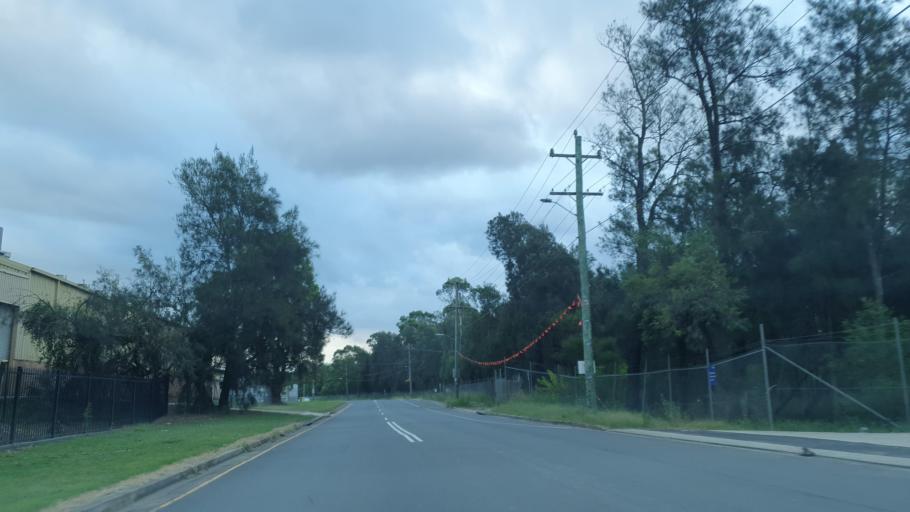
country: AU
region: New South Wales
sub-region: Penrith Municipality
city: Werrington County
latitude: -33.7395
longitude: 150.7740
